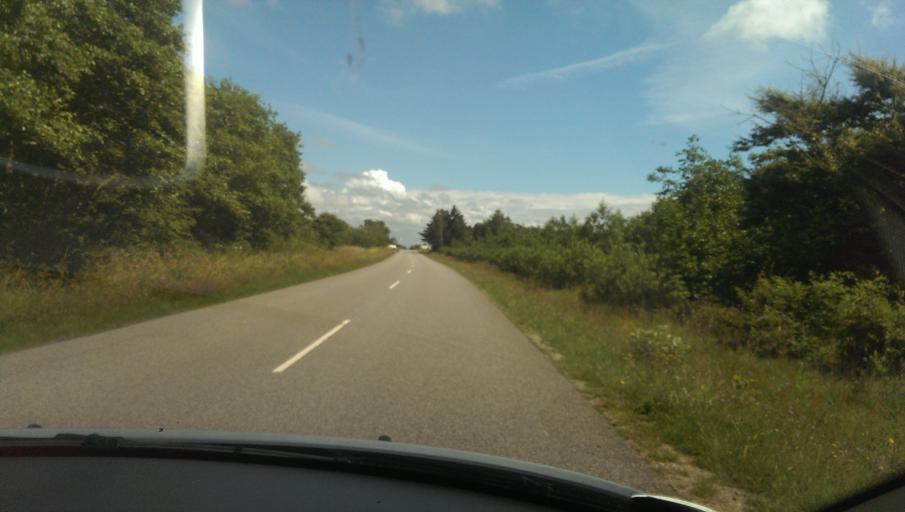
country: DK
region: Central Jutland
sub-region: Ringkobing-Skjern Kommune
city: Ringkobing
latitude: 56.1404
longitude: 8.1505
